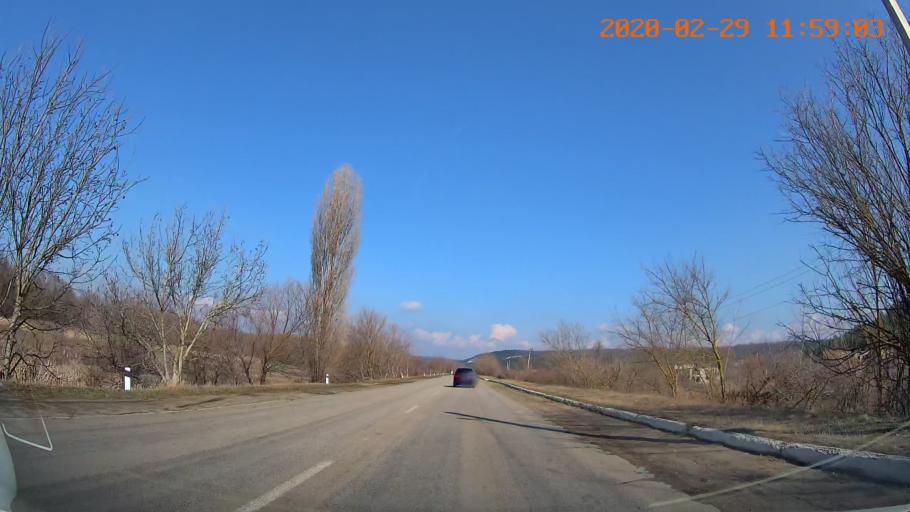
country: MD
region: Telenesti
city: Ribnita
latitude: 47.8205
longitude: 29.0146
